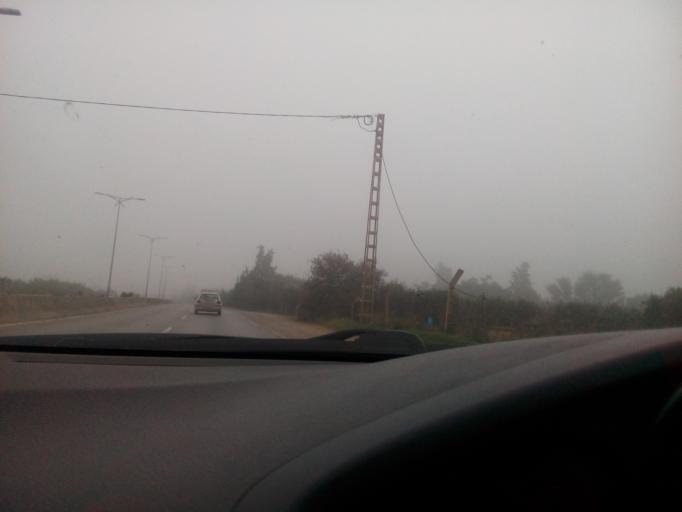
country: DZ
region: Oran
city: Bou Tlelis
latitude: 35.5727
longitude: -0.8629
